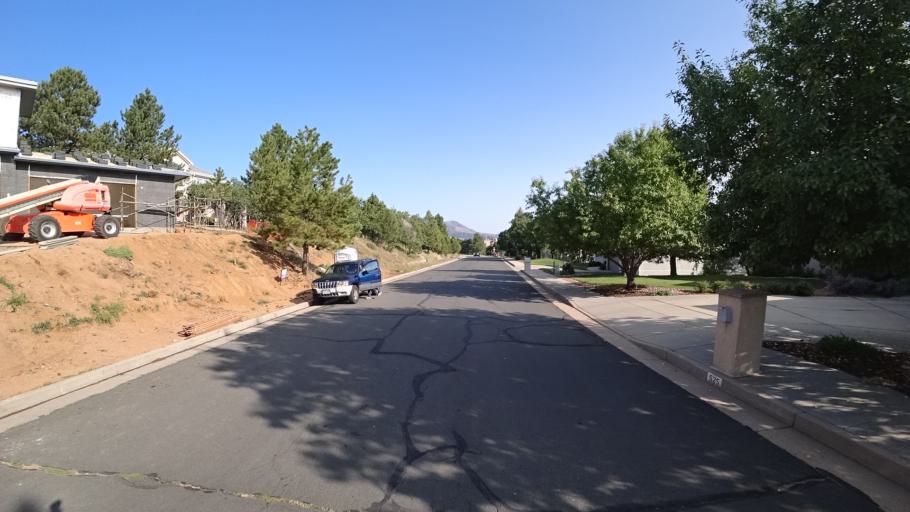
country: US
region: Colorado
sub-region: El Paso County
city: Colorado Springs
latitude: 38.8207
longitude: -104.8749
